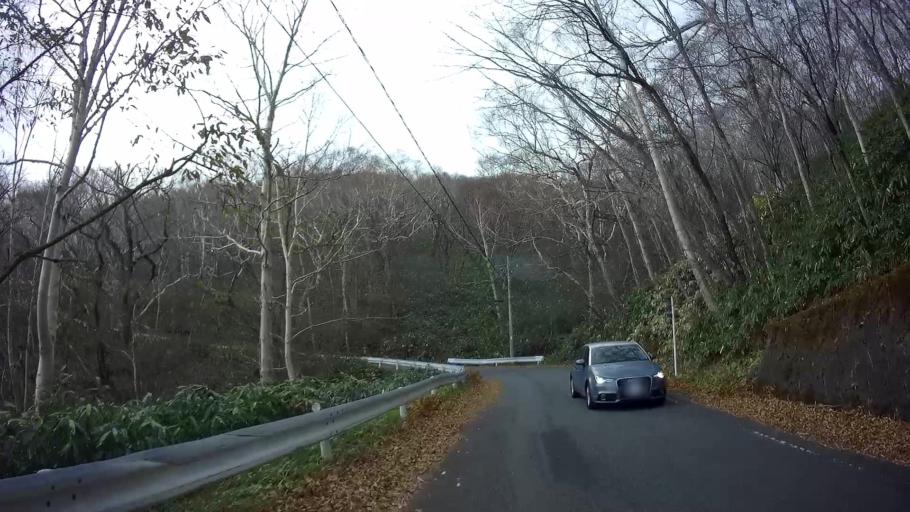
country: JP
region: Gunma
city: Nakanojomachi
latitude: 36.6887
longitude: 138.6527
